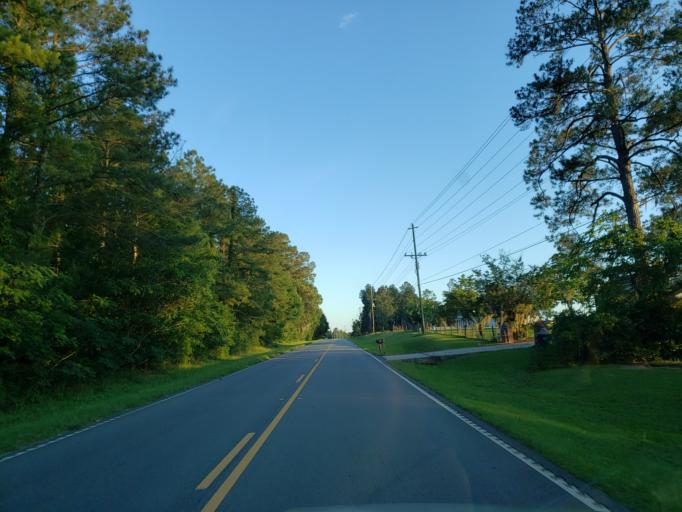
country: US
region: Georgia
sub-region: Lowndes County
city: Valdosta
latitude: 30.7073
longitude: -83.2416
